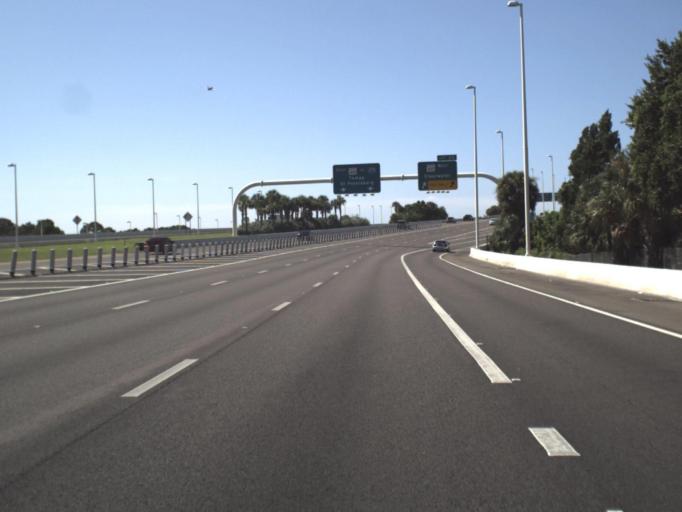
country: US
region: Florida
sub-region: Hillsborough County
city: Town 'n' Country
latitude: 27.9727
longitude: -82.5470
